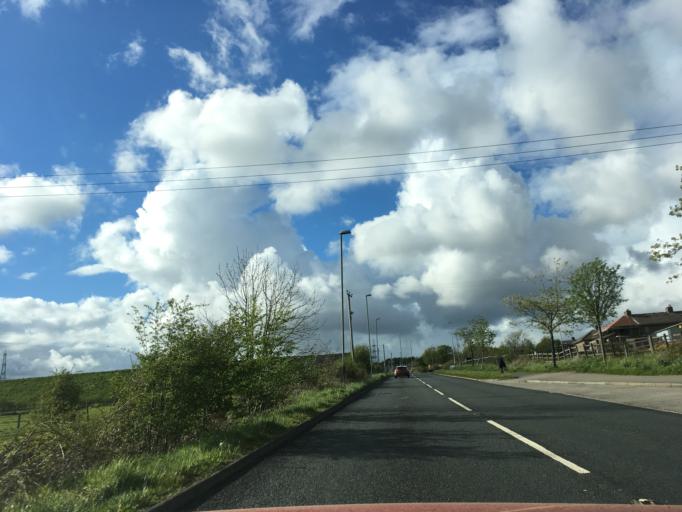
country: GB
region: Wales
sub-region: Caerphilly County Borough
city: Rhymney
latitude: 51.7723
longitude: -3.3001
